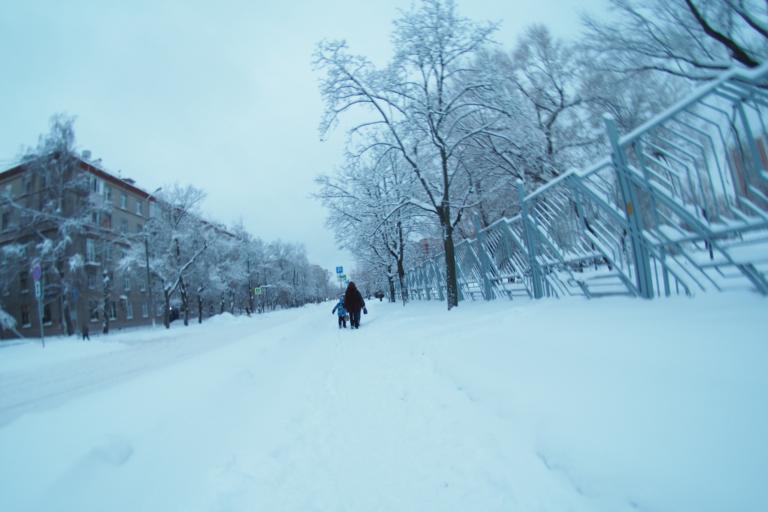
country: RU
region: Moscow
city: Ryazanskiy
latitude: 55.7442
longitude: 37.7738
